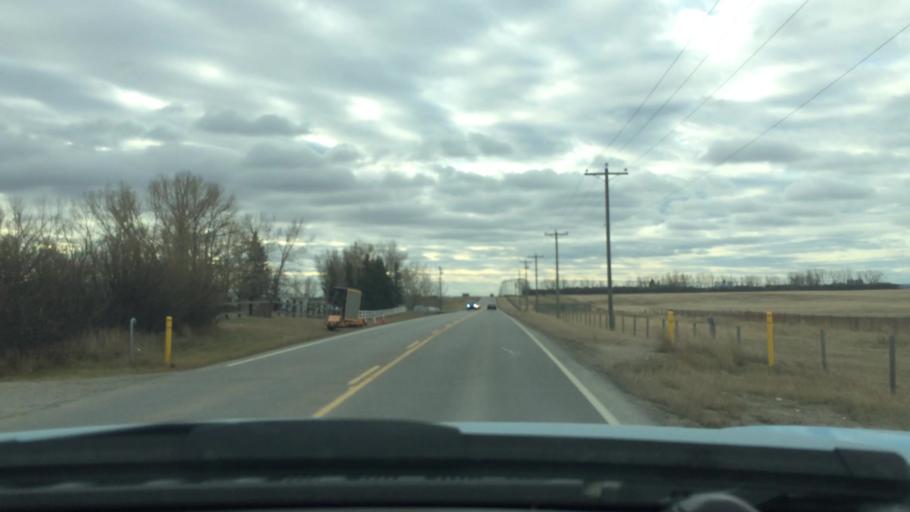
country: CA
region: Alberta
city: Airdrie
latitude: 51.2334
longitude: -114.0250
